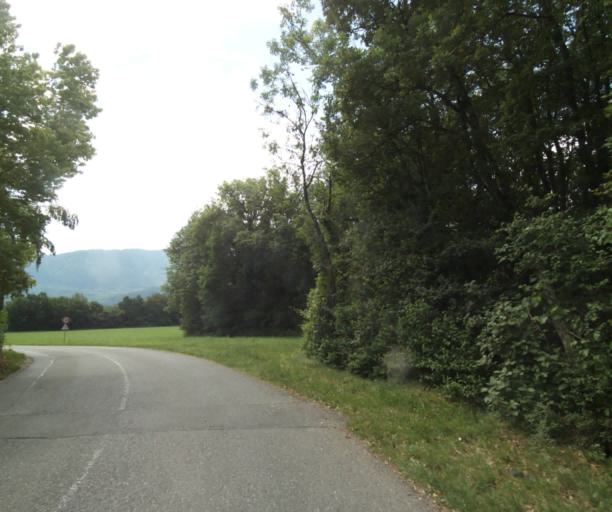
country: FR
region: Rhone-Alpes
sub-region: Departement de la Haute-Savoie
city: Thonon-les-Bains
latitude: 46.3485
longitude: 6.4954
